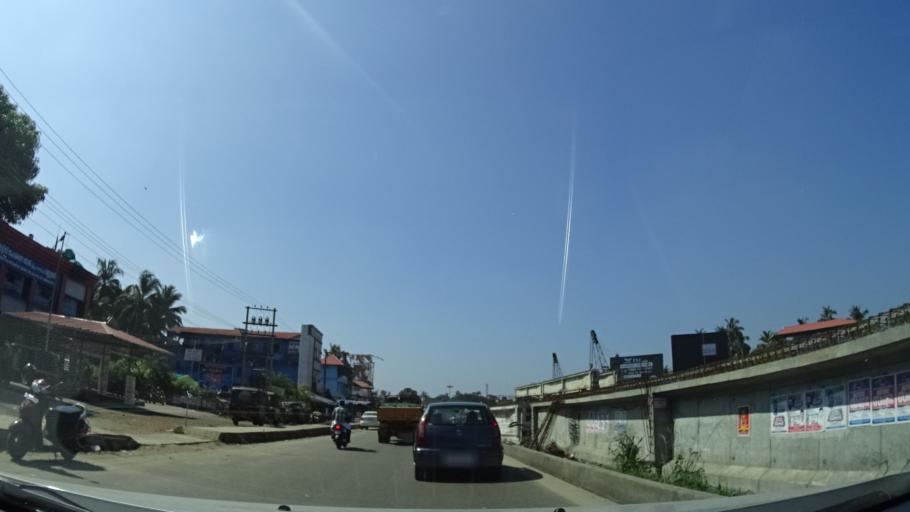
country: IN
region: Kerala
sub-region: Thrissur District
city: Trichur
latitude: 10.5326
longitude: 76.2611
